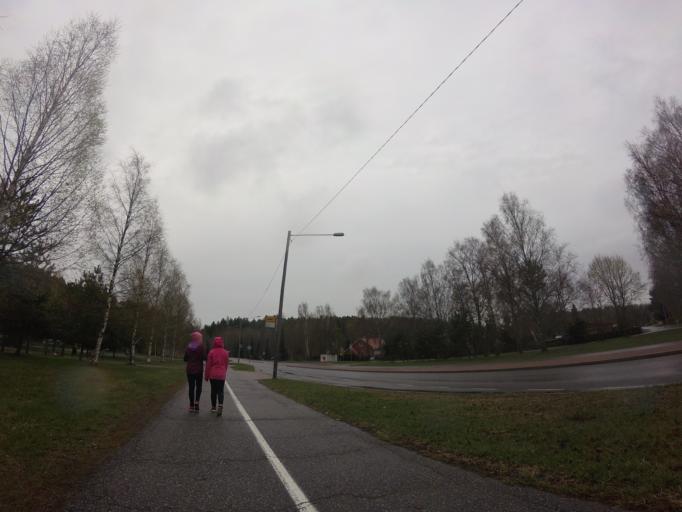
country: FI
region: Varsinais-Suomi
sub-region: Turku
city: Raisio
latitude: 60.4522
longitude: 22.1589
